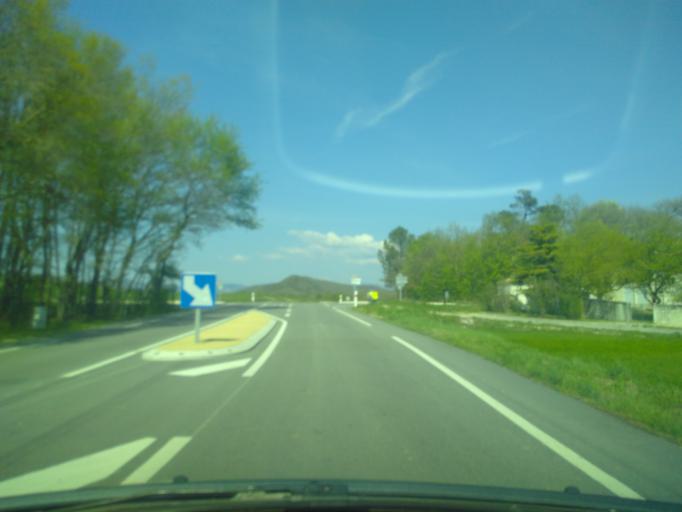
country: FR
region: Rhone-Alpes
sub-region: Departement de la Drome
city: Crest
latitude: 44.6674
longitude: 5.0050
